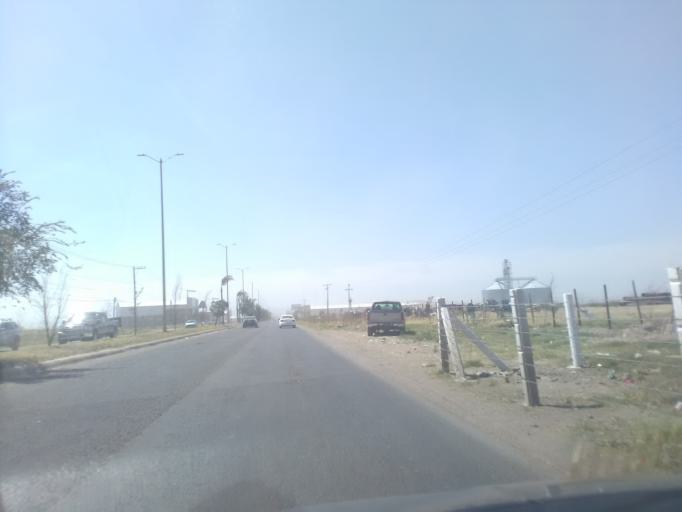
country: MX
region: Durango
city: Victoria de Durango
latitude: 24.0291
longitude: -104.5998
